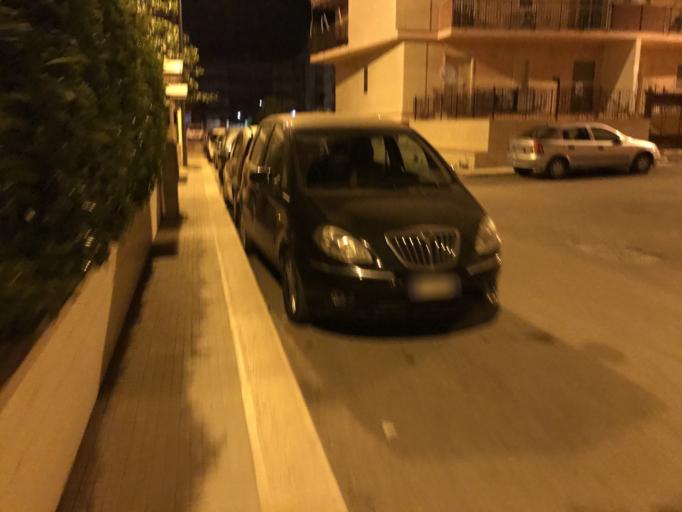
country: IT
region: Apulia
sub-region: Provincia di Bari
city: Corato
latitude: 41.1537
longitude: 16.4024
